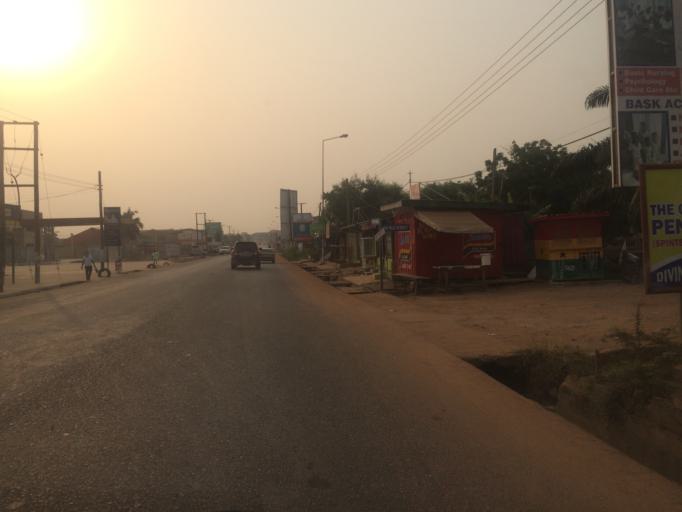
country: GH
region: Greater Accra
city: Nungua
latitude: 5.6406
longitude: -0.1080
